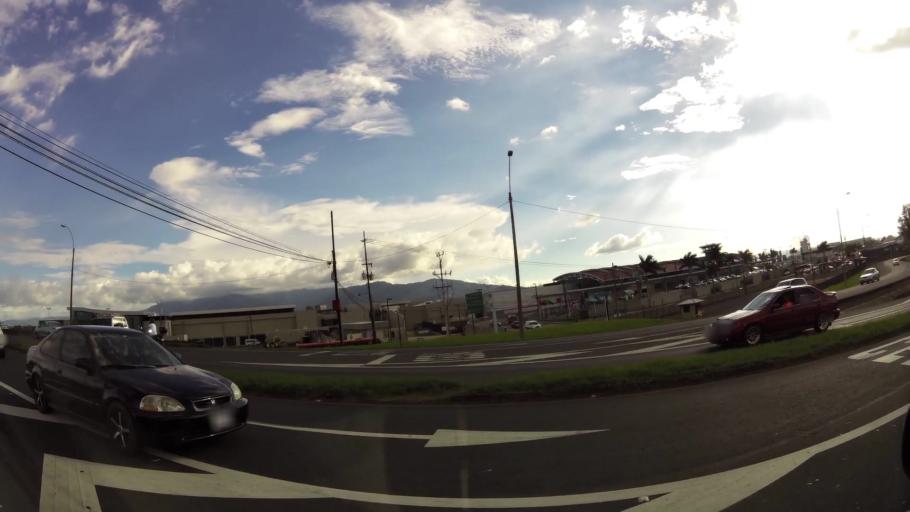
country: CR
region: Alajuela
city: Alajuela
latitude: 10.0001
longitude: -84.2029
